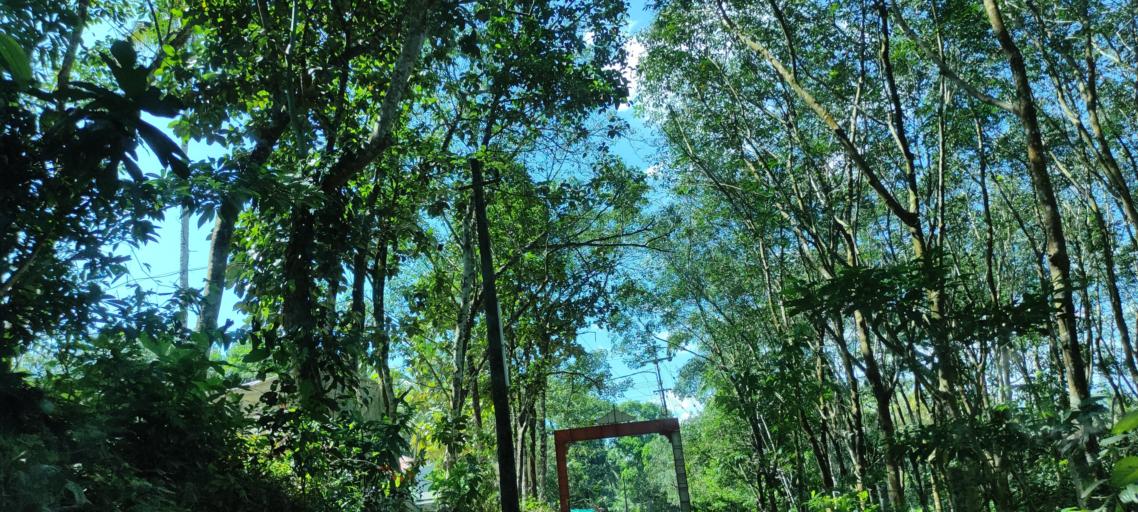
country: IN
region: Kerala
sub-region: Pattanamtitta
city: Adur
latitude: 9.0896
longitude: 76.6979
